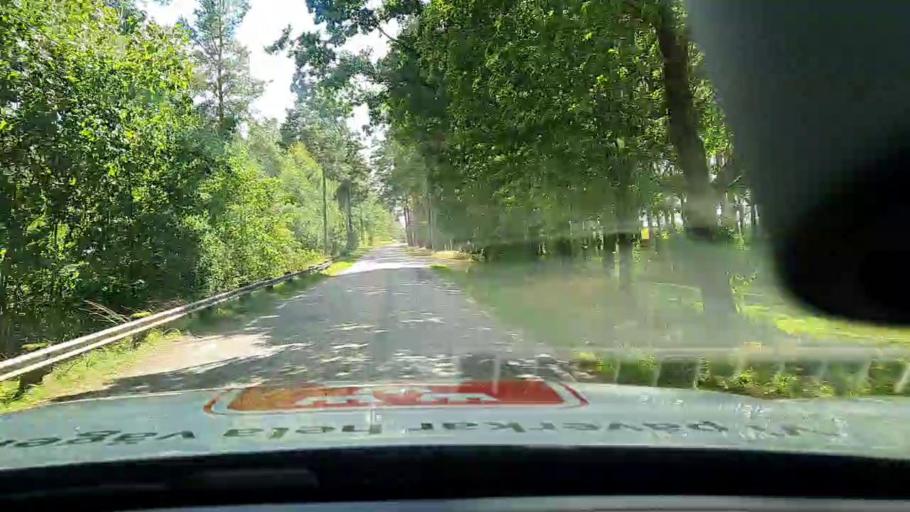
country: SE
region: Vaestra Goetaland
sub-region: Toreboda Kommun
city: Toereboda
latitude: 58.5764
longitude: 14.1238
